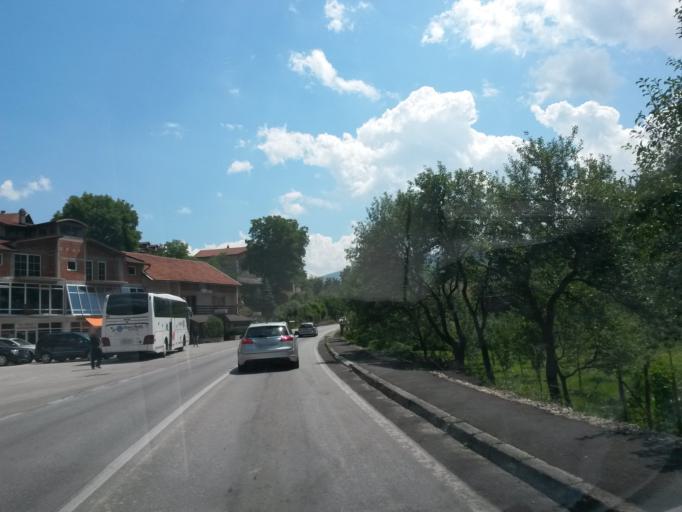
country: BA
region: Federation of Bosnia and Herzegovina
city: Turbe
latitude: 44.2439
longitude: 17.5972
